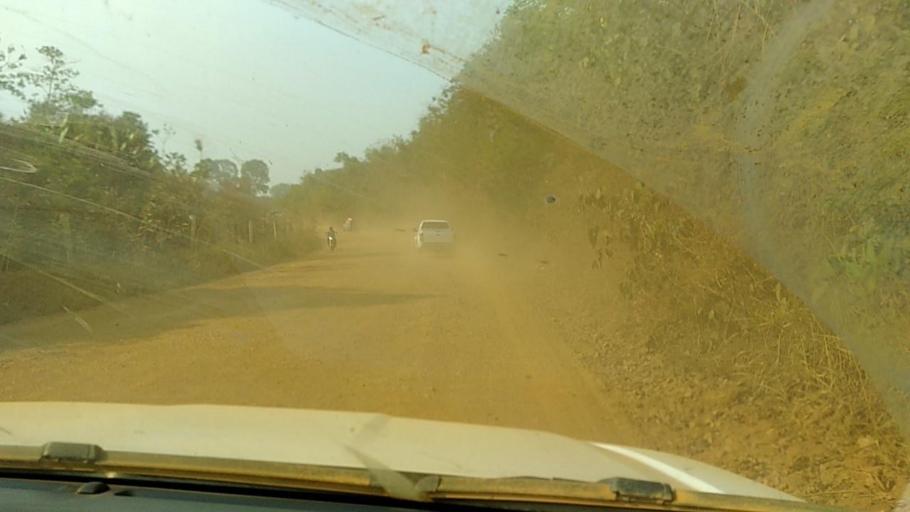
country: BR
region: Rondonia
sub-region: Porto Velho
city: Porto Velho
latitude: -8.7466
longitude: -63.9645
